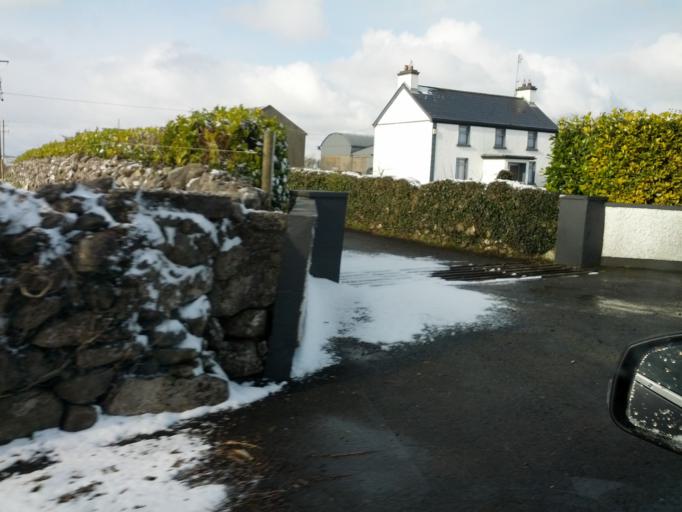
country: IE
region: Connaught
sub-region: County Galway
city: Athenry
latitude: 53.1862
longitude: -8.7692
